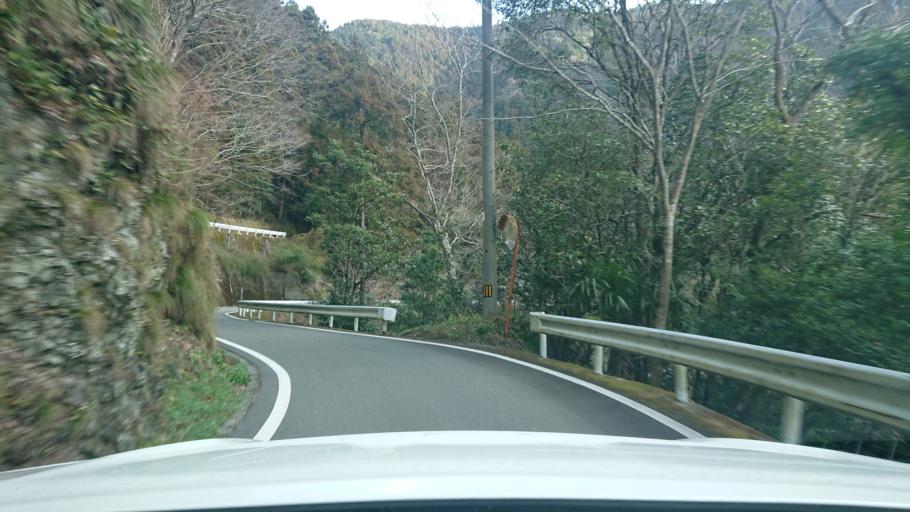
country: JP
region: Tokushima
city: Kamojimacho-jogejima
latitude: 33.9047
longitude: 134.3949
